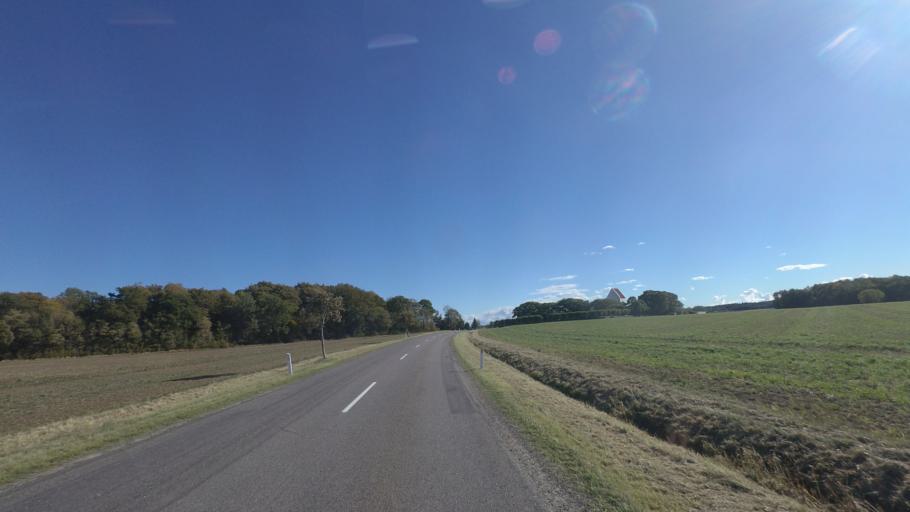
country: DK
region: Capital Region
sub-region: Bornholm Kommune
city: Nexo
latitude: 55.1196
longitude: 15.1035
